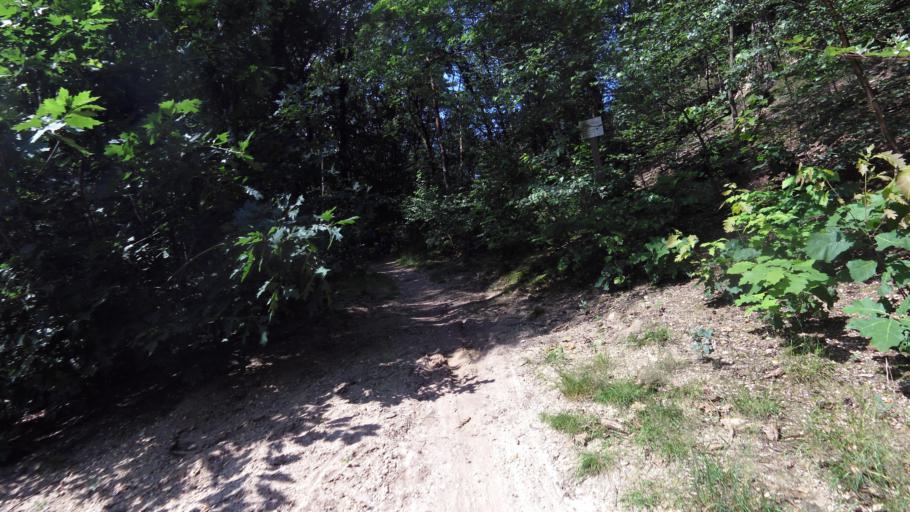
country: NL
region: Gelderland
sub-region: Gemeente Renkum
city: Oosterbeek
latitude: 51.9980
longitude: 5.8320
